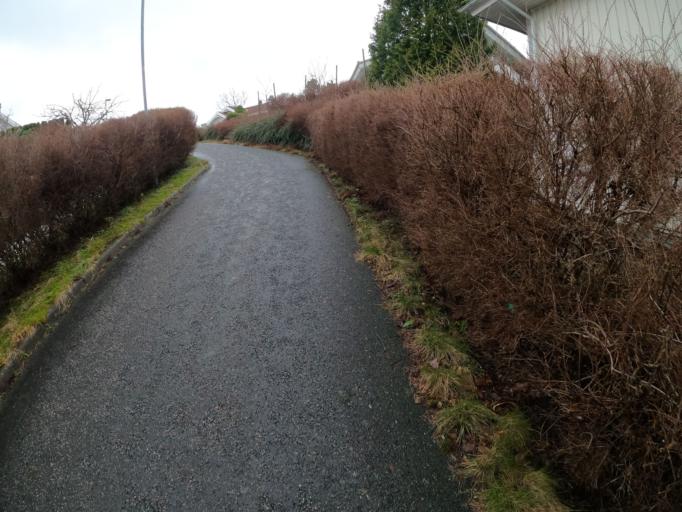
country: SE
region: Vaestra Goetaland
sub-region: Harryda Kommun
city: Molnlycke
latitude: 57.6454
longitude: 12.1038
